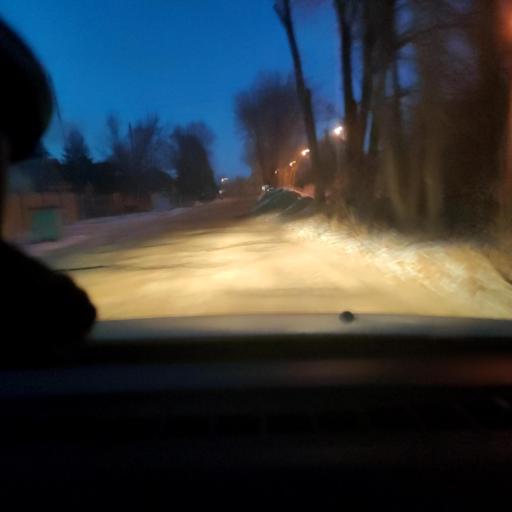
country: RU
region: Samara
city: Petra-Dubrava
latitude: 53.2553
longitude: 50.3389
